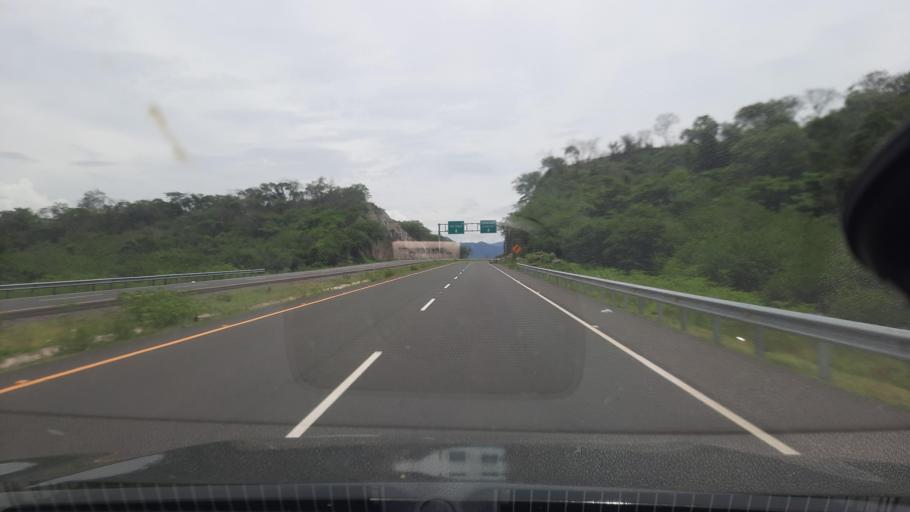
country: HN
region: Valle
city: Aramecina
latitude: 13.7344
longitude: -87.7191
